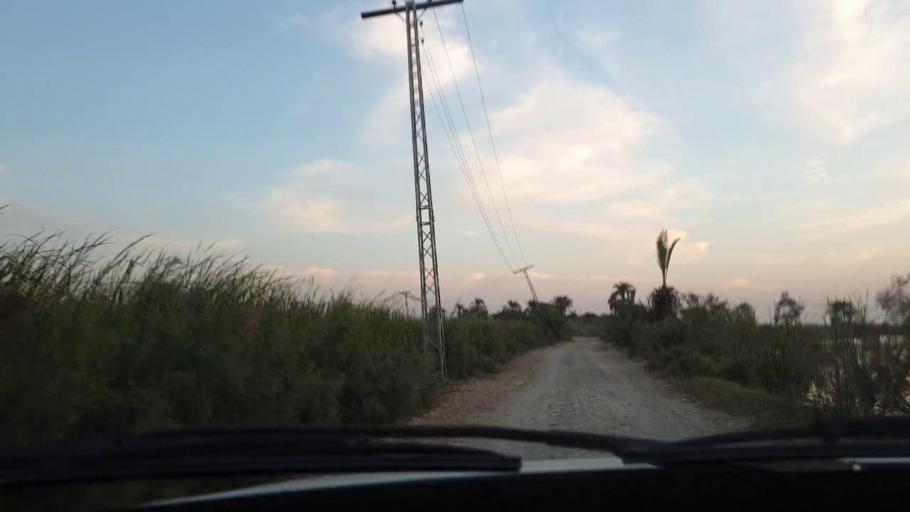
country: PK
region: Sindh
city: Tando Muhammad Khan
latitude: 25.0931
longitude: 68.3923
